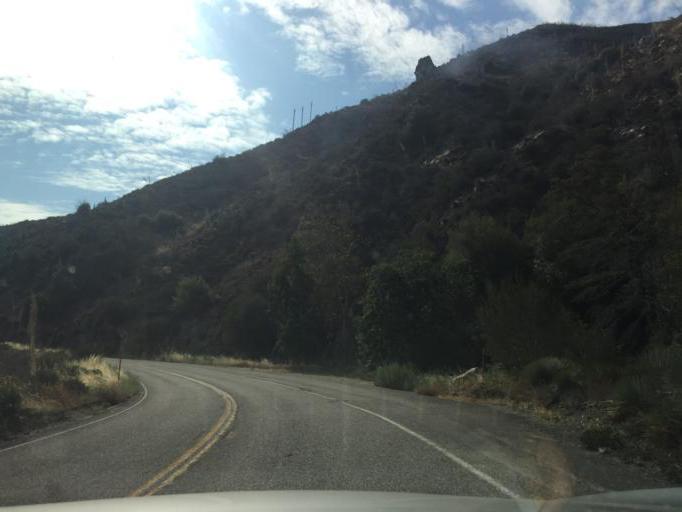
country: US
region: California
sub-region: Los Angeles County
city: Altadena
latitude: 34.2699
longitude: -118.0750
